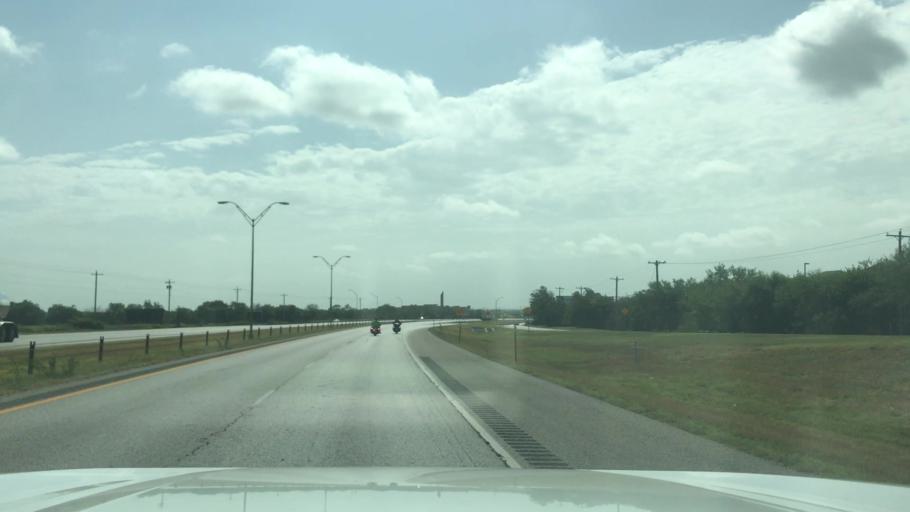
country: US
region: Texas
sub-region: Taylor County
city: Abilene
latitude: 32.4900
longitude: -99.7223
